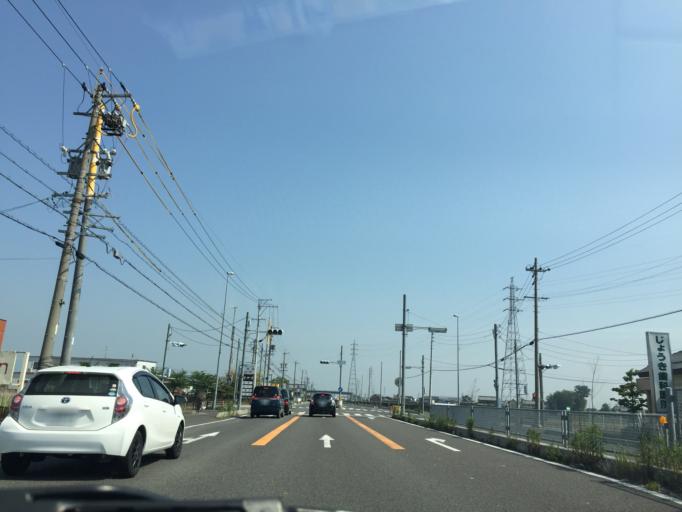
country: JP
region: Gifu
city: Ogaki
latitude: 35.2590
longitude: 136.6017
